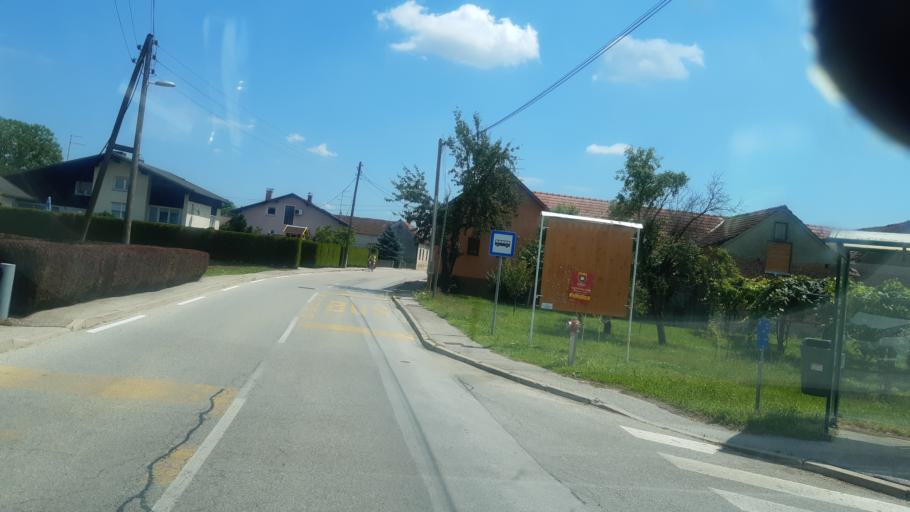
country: SI
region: Moravske Toplice
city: Moravske Toplice
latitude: 46.6694
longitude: 16.2203
